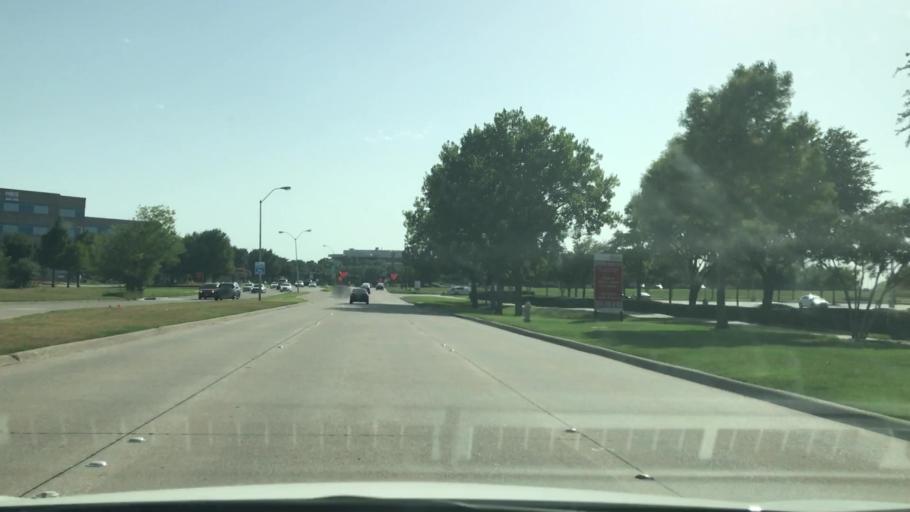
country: US
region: Texas
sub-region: Dallas County
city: Richardson
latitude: 32.9985
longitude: -96.7515
